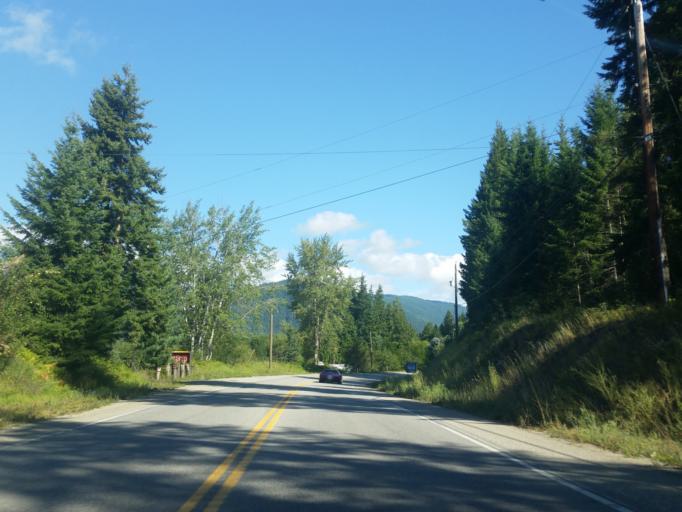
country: CA
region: British Columbia
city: Sicamous
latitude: 50.6929
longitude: -119.0422
